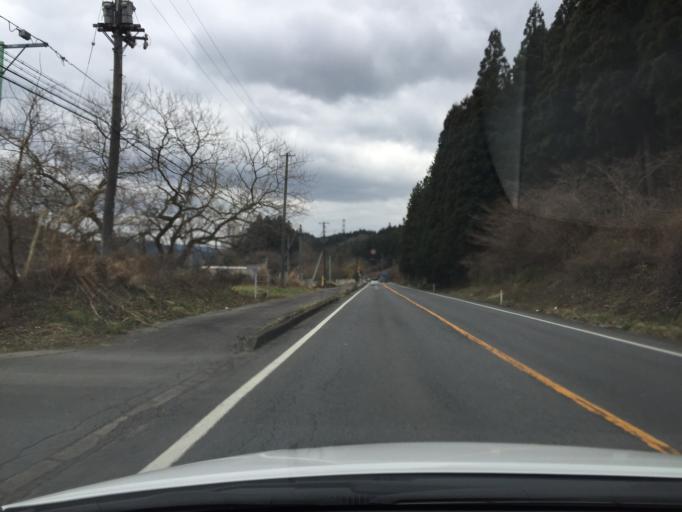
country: JP
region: Fukushima
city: Iwaki
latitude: 37.1392
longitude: 140.6912
